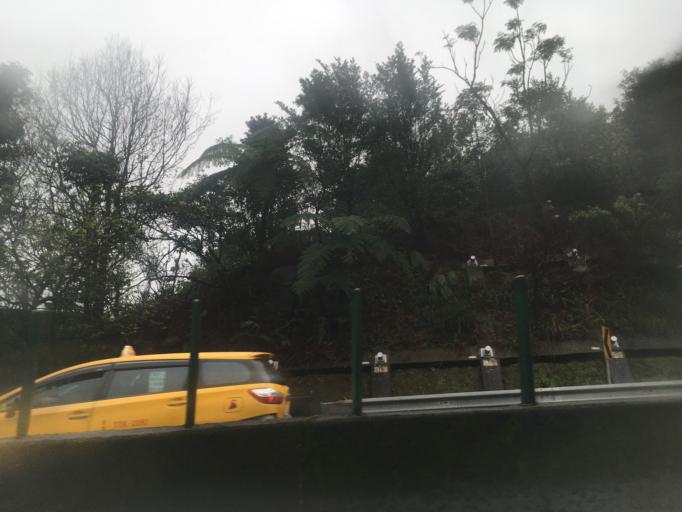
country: TW
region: Taiwan
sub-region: Keelung
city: Keelung
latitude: 25.1133
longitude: 121.6902
